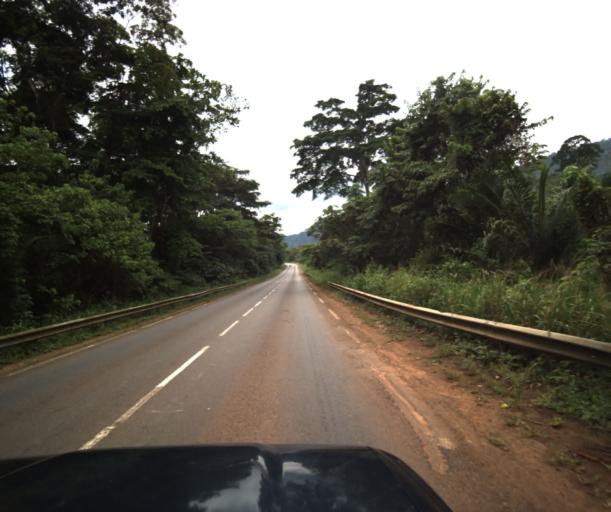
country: CM
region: Centre
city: Eseka
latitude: 3.8907
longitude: 10.7835
